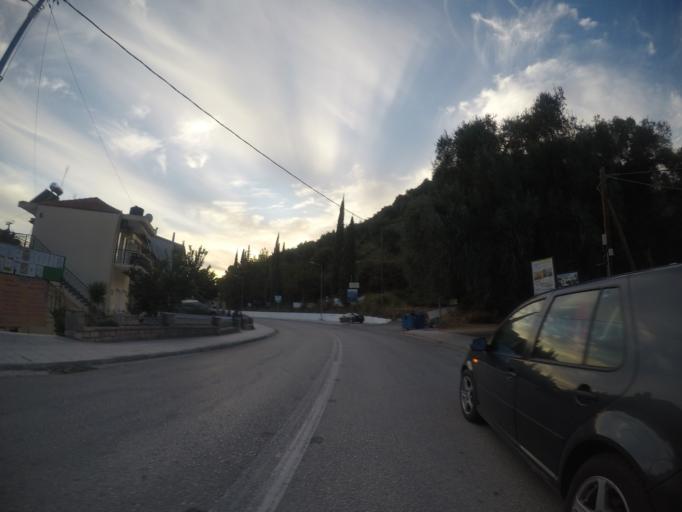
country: GR
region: Epirus
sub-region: Nomos Prevezis
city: Parga
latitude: 39.2847
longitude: 20.4095
